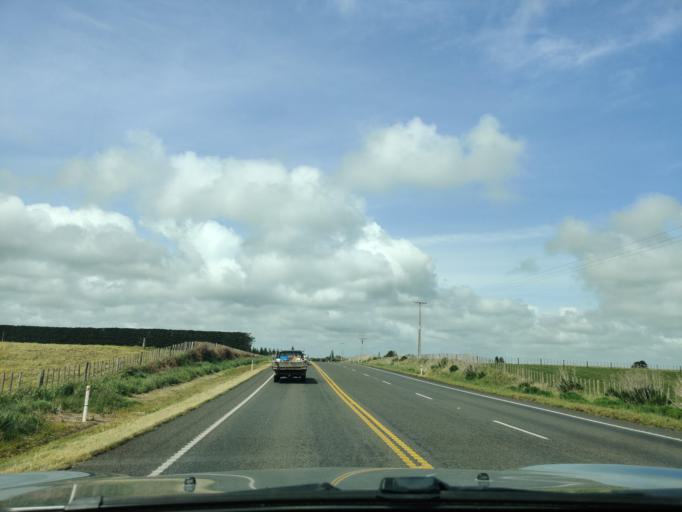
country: NZ
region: Taranaki
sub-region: South Taranaki District
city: Patea
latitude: -39.7656
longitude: 174.6164
